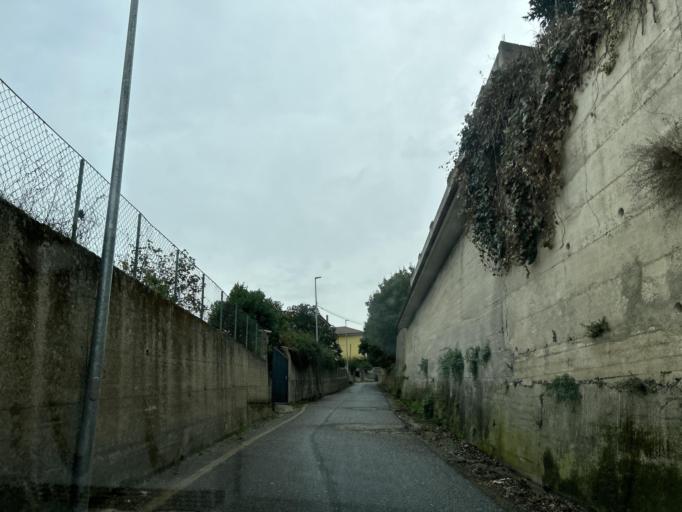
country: IT
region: Calabria
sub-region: Provincia di Catanzaro
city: Staletti
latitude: 38.7663
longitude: 16.5369
